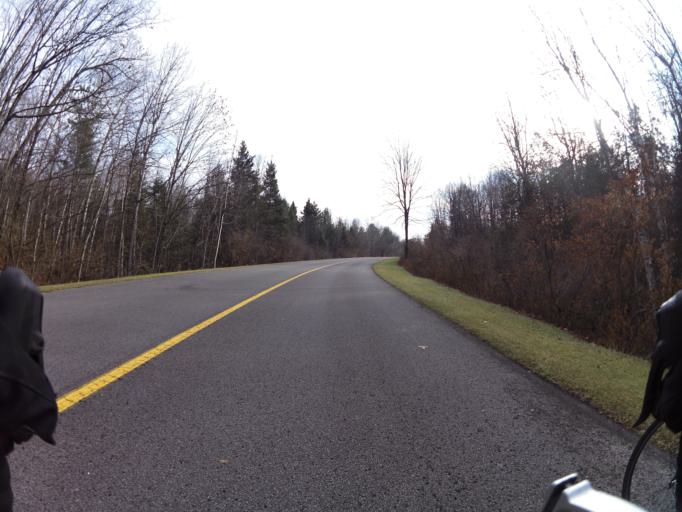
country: CA
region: Quebec
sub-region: Outaouais
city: Gatineau
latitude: 45.4568
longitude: -75.7877
